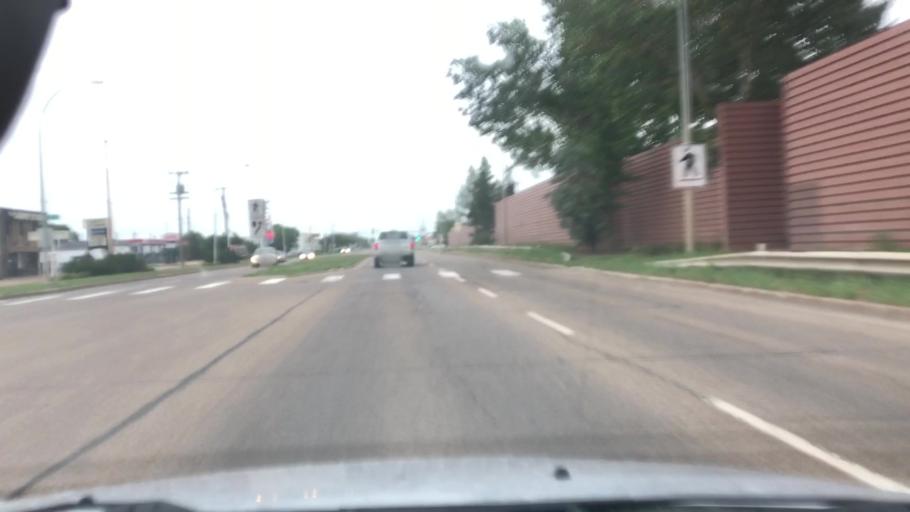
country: CA
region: Alberta
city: St. Albert
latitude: 53.5589
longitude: -113.5944
